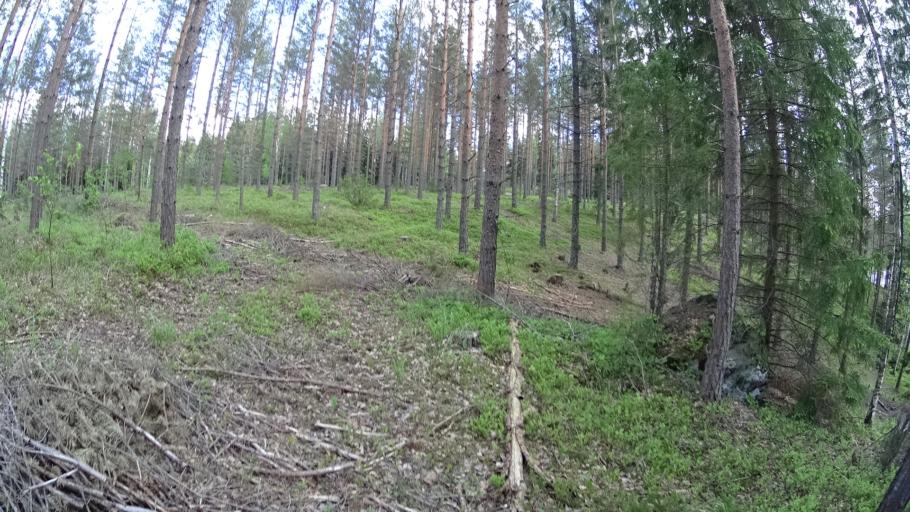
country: FI
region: Varsinais-Suomi
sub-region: Salo
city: Kisko
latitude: 60.1871
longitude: 23.5490
